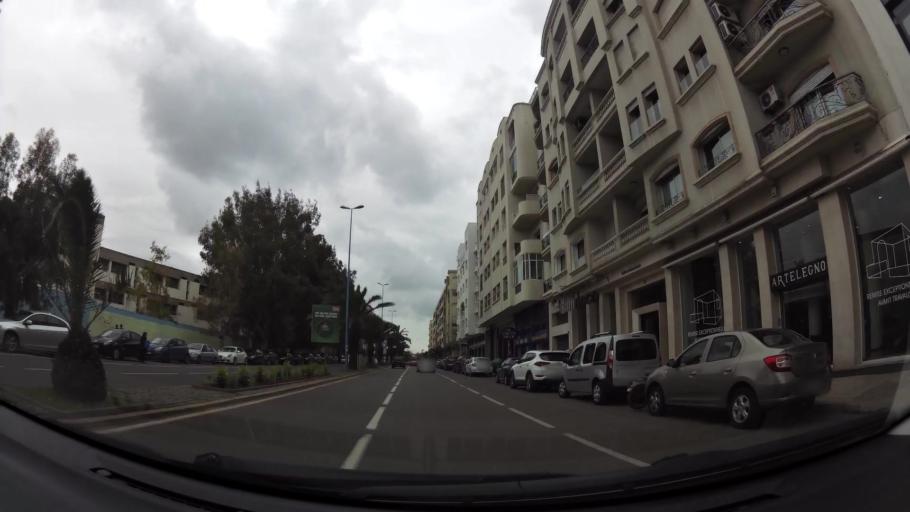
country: MA
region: Grand Casablanca
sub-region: Casablanca
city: Casablanca
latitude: 33.5915
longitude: -7.6425
